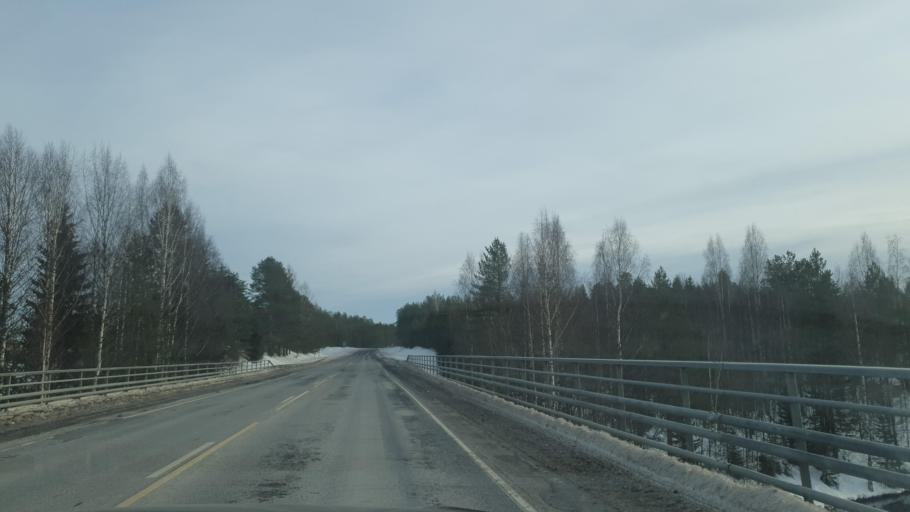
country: FI
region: Northern Ostrobothnia
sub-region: Oulunkaari
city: Utajaervi
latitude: 64.6460
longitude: 26.5745
